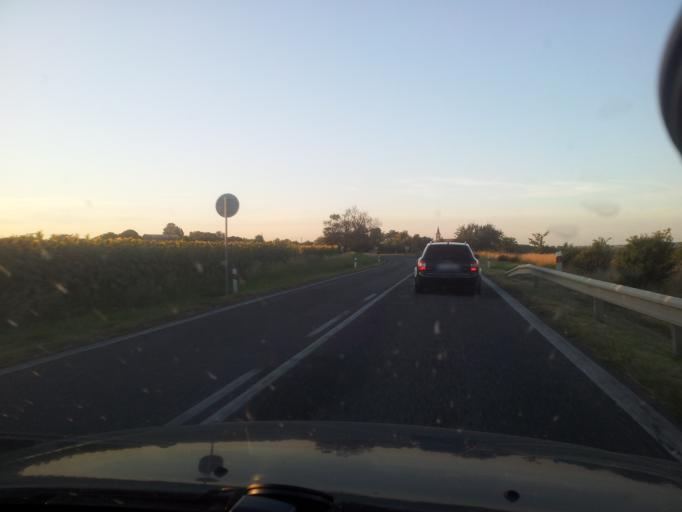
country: SK
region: Nitriansky
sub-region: Okres Nove Zamky
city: Sturovo
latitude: 47.8806
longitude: 18.6427
